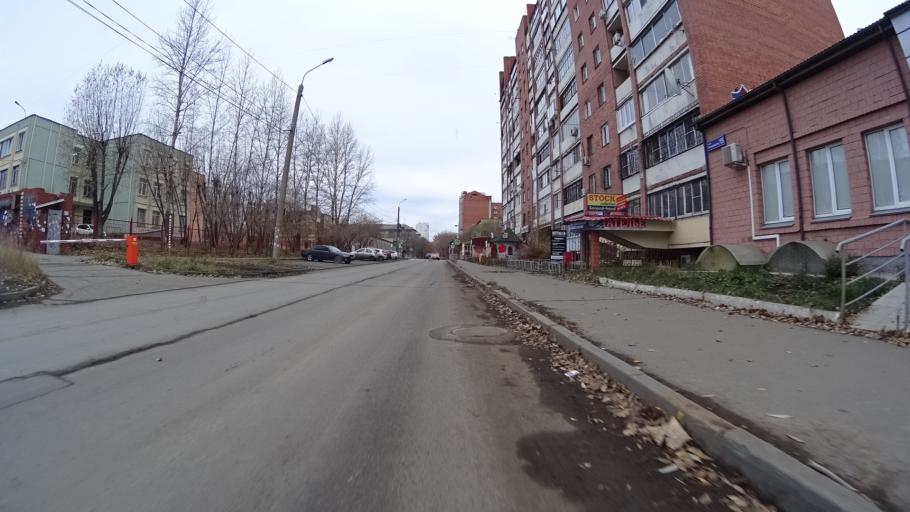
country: RU
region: Chelyabinsk
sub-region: Gorod Chelyabinsk
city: Chelyabinsk
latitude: 55.1537
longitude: 61.3775
